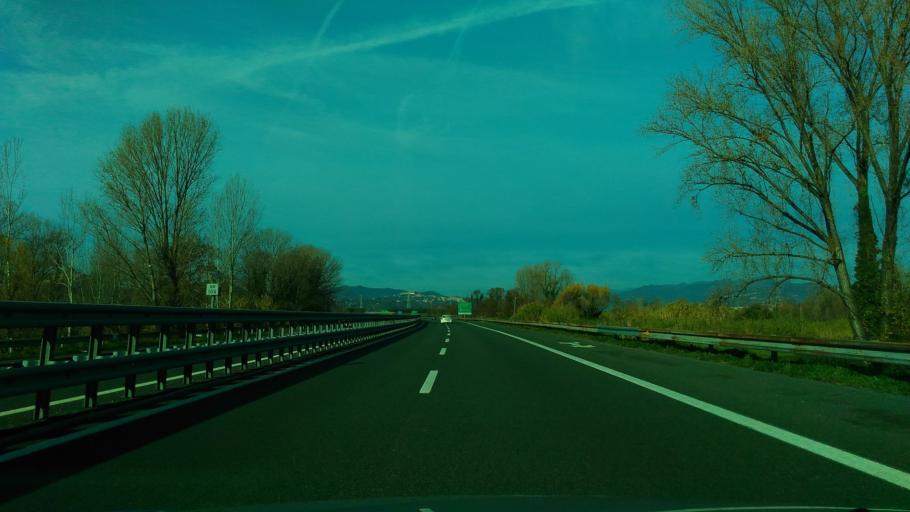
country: IT
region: Liguria
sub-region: Provincia di La Spezia
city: Sarzana
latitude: 44.0946
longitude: 9.9651
